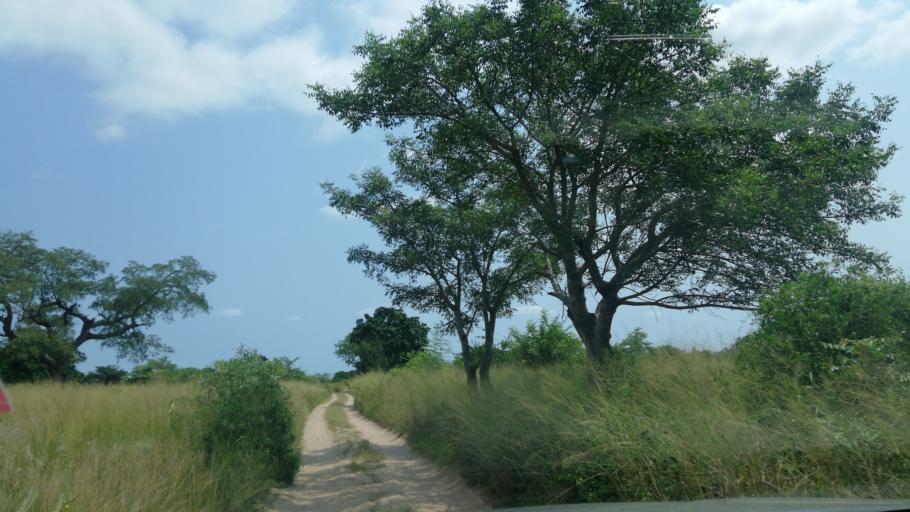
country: MZ
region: Maputo
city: Matola
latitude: -26.1101
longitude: 32.4242
